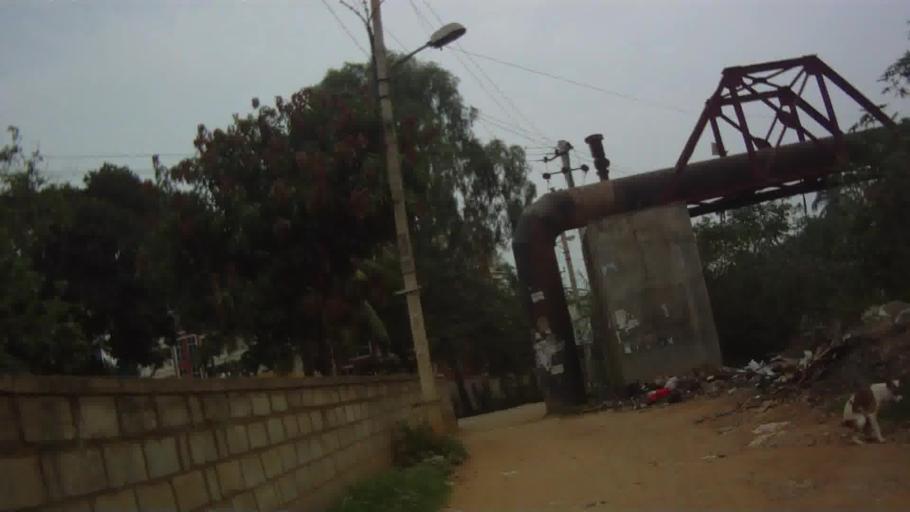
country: IN
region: Karnataka
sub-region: Bangalore Urban
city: Bangalore
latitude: 12.9672
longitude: 77.7034
